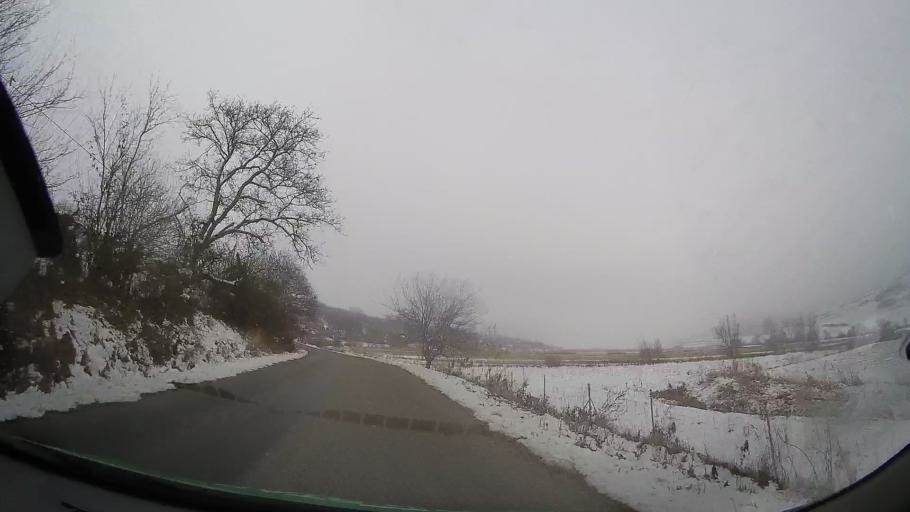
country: RO
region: Bacau
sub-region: Comuna Vultureni
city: Vultureni
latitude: 46.3614
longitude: 27.2869
